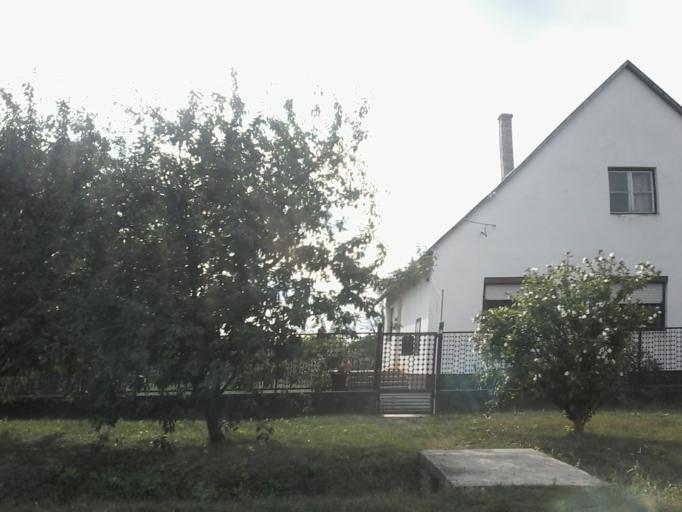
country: HU
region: Vas
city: Janoshaza
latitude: 47.0573
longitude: 17.1380
